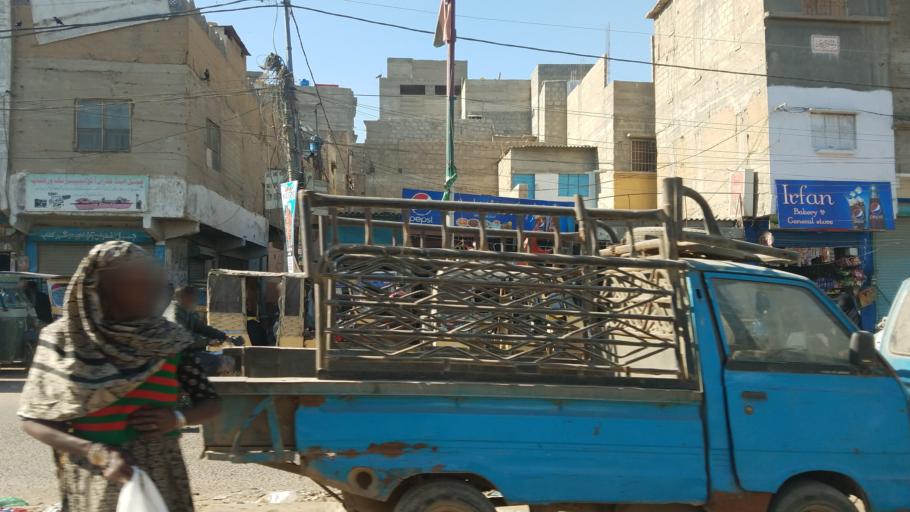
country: PK
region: Sindh
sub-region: Karachi District
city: Karachi
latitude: 24.9214
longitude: 67.0504
